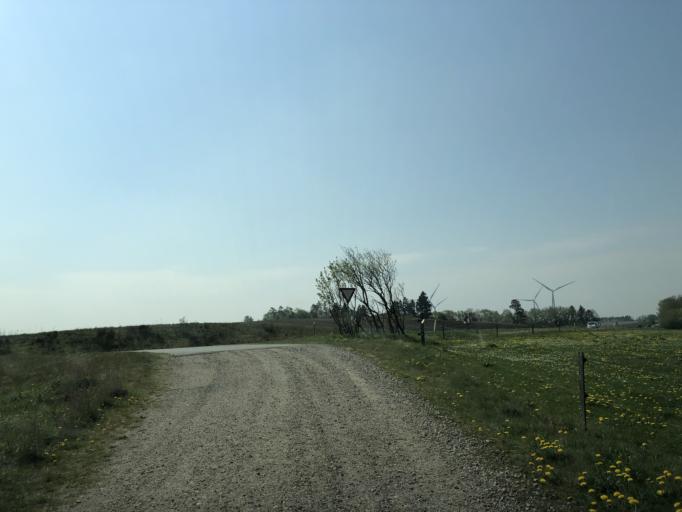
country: DK
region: Central Jutland
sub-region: Holstebro Kommune
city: Holstebro
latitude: 56.3299
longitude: 8.4806
